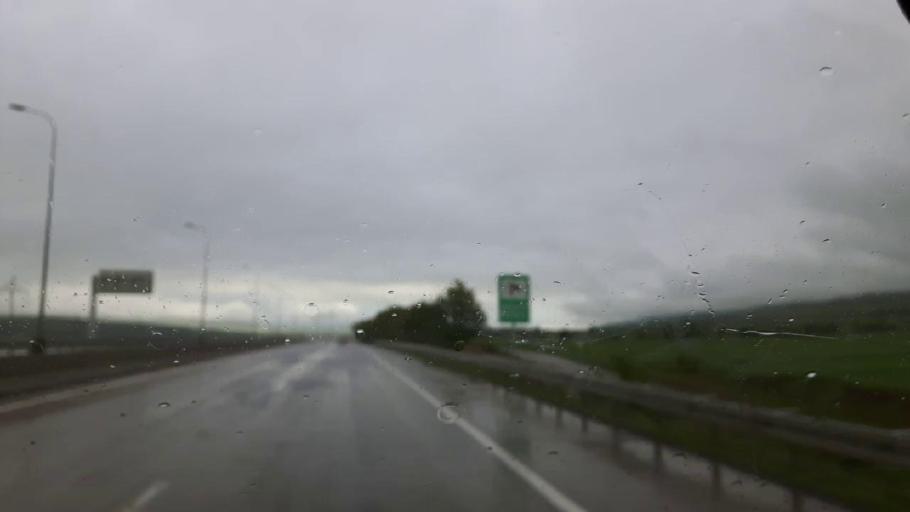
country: GE
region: Shida Kartli
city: Kaspi
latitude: 42.0185
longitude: 44.3134
